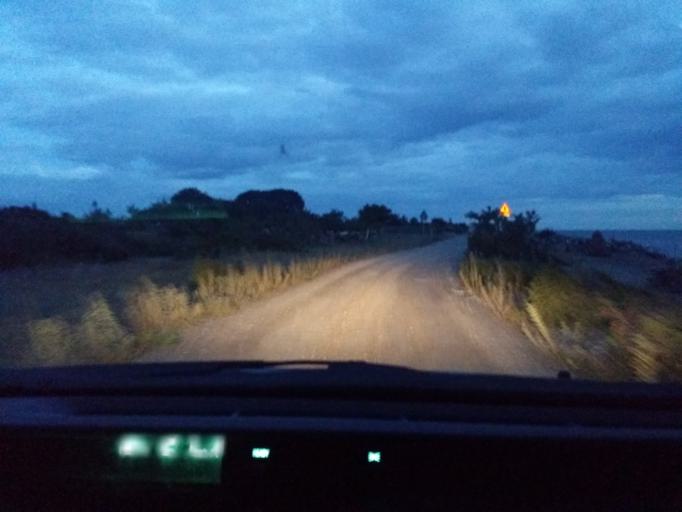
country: SE
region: Kalmar
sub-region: Borgholms Kommun
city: Borgholm
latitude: 57.1499
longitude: 16.9155
